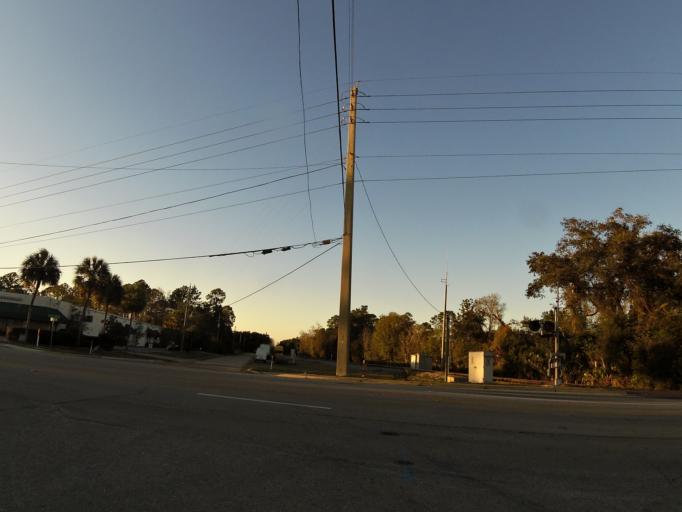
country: US
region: Florida
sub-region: Saint Johns County
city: Fruit Cove
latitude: 30.2060
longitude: -81.5789
